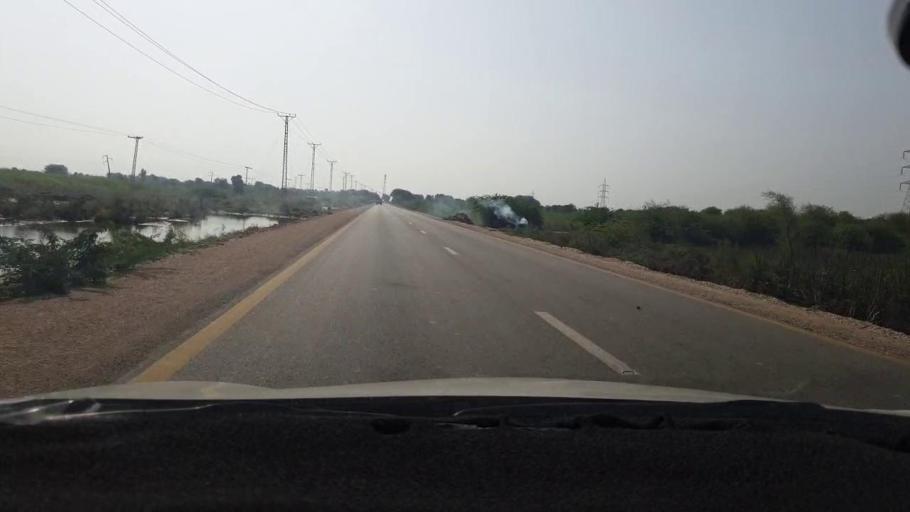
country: PK
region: Sindh
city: Jhol
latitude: 25.9464
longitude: 68.9826
